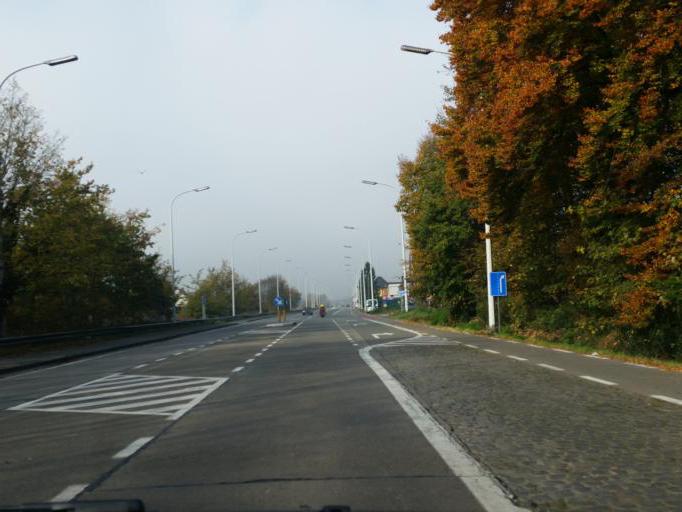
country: BE
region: Flanders
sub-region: Provincie Oost-Vlaanderen
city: Evergem
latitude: 51.0785
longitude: 3.6770
